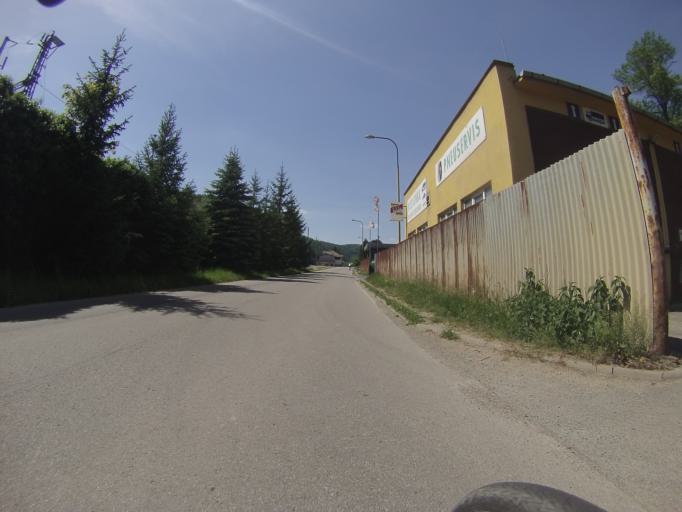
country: CZ
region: South Moravian
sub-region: Okres Blansko
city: Adamov
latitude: 49.2945
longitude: 16.6666
